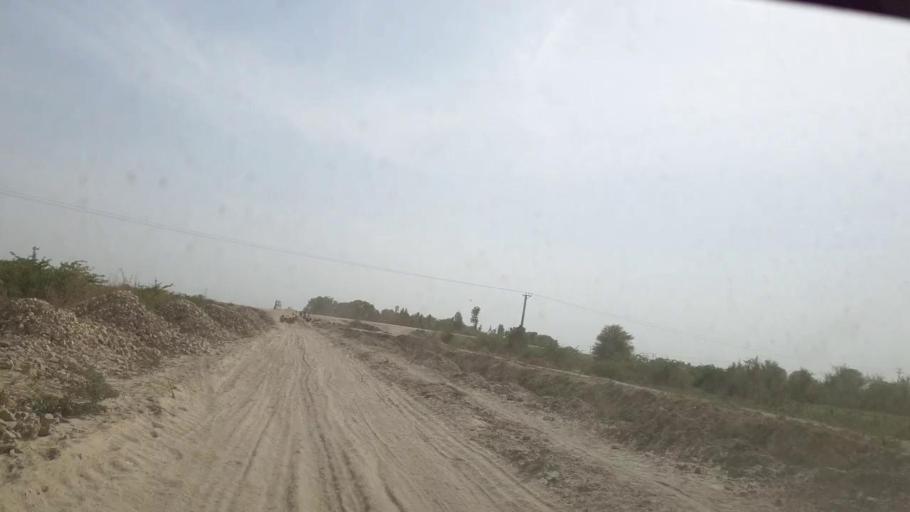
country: PK
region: Sindh
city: Nabisar
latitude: 25.0590
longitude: 69.5772
